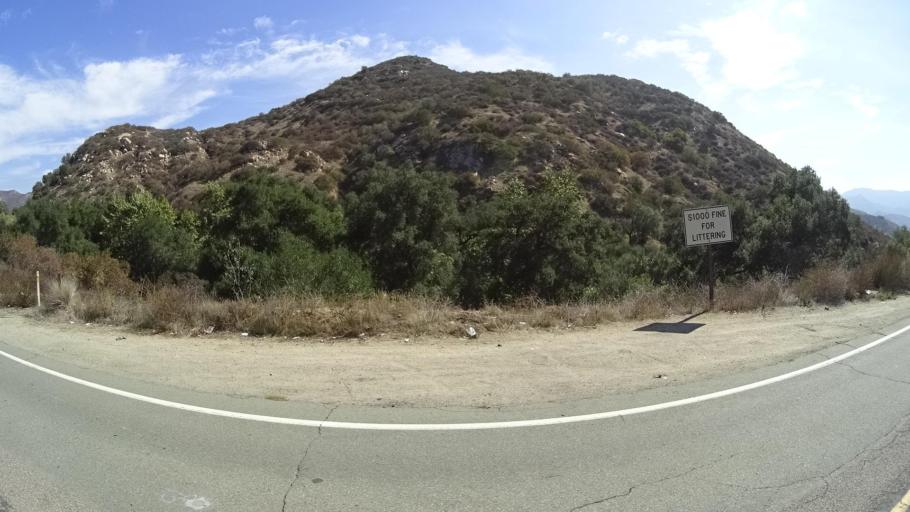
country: US
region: California
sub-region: San Diego County
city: Harbison Canyon
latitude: 32.8113
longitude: -116.8429
